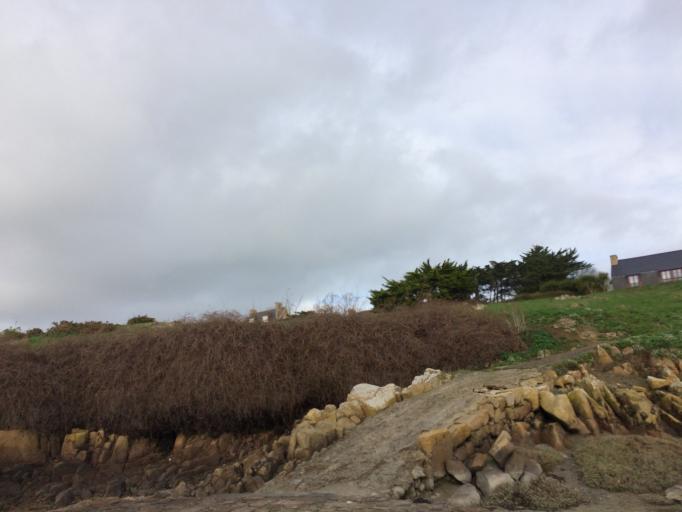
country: FR
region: Brittany
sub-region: Departement des Cotes-d'Armor
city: Ploubazlanec
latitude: 48.8474
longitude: -3.0098
